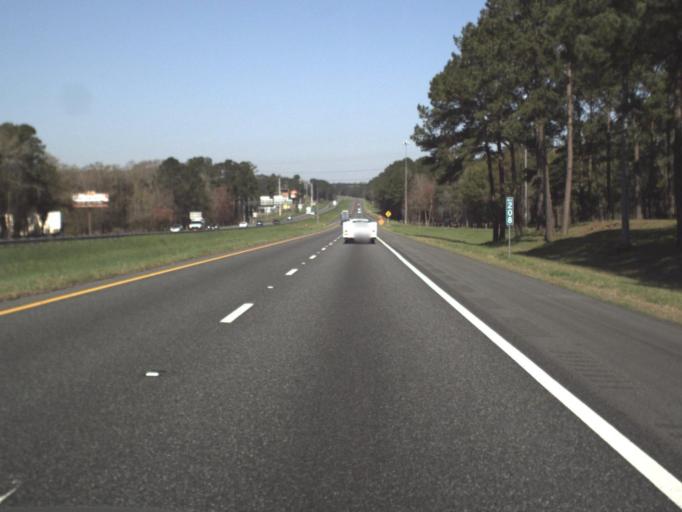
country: US
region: Florida
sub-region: Leon County
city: Tallahassee
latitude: 30.4866
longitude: -84.1603
